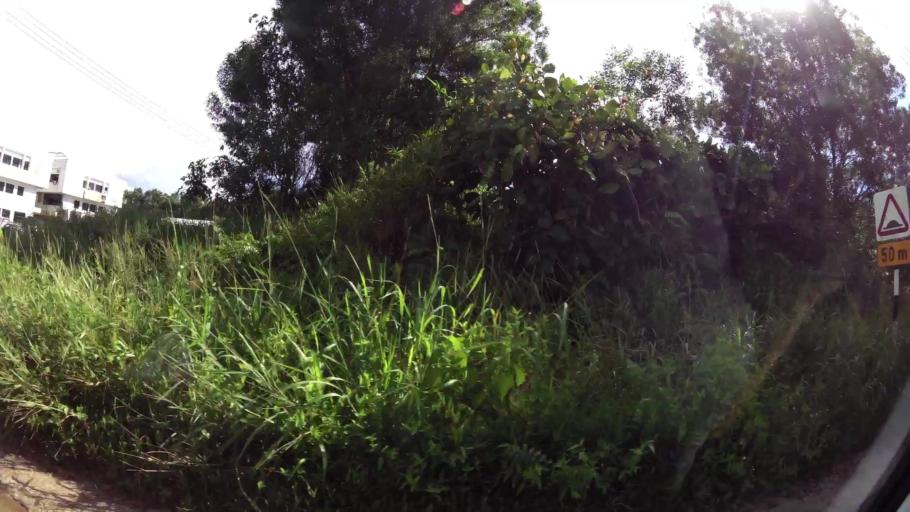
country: BN
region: Brunei and Muara
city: Bandar Seri Begawan
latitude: 5.0129
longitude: 115.0334
